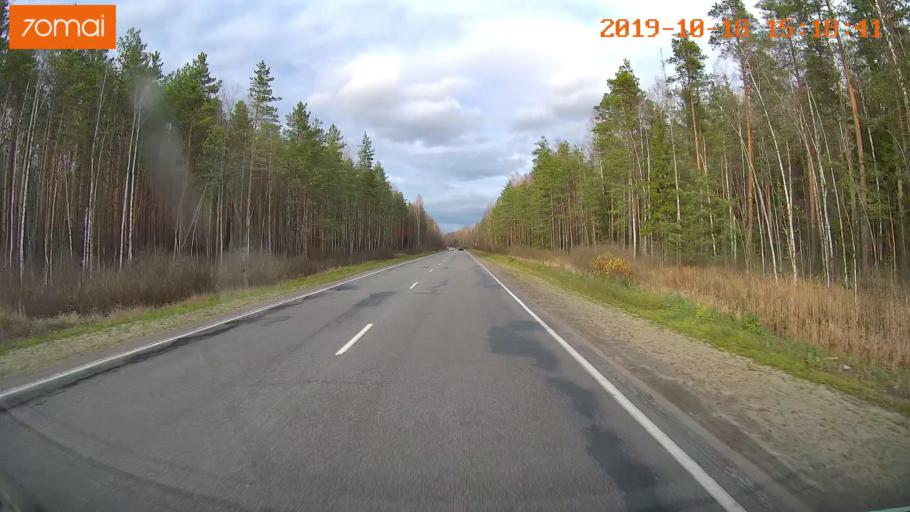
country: RU
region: Vladimir
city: Anopino
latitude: 55.6625
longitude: 40.7312
